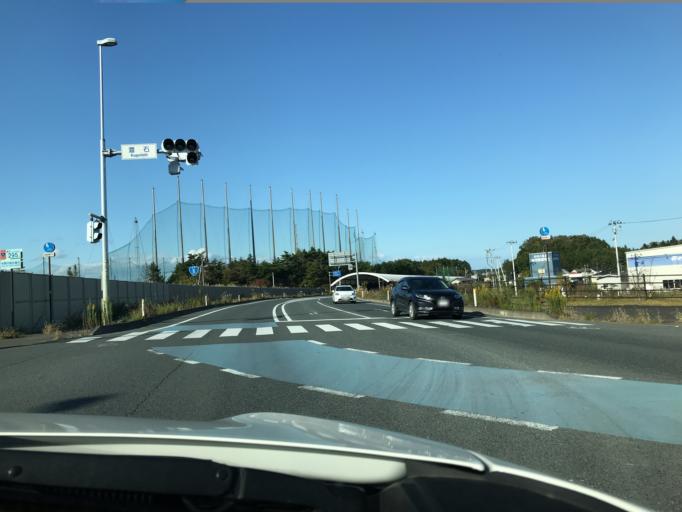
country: JP
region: Miyagi
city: Marumori
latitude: 37.7780
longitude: 140.9398
